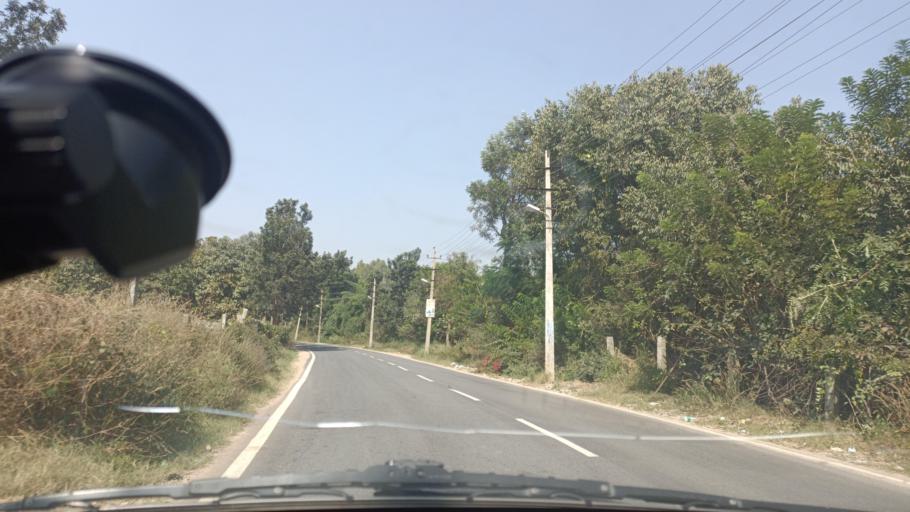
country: IN
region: Karnataka
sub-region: Bangalore Rural
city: Devanhalli
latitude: 13.1989
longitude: 77.6459
